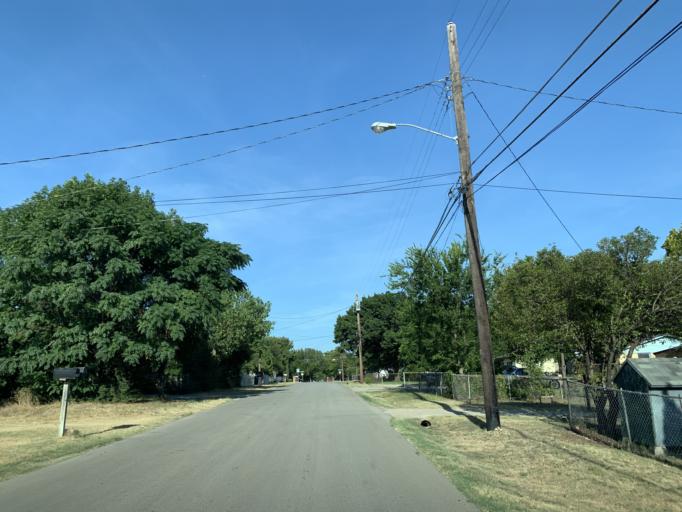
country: US
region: Texas
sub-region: Dallas County
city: Cockrell Hill
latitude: 32.7120
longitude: -96.9018
